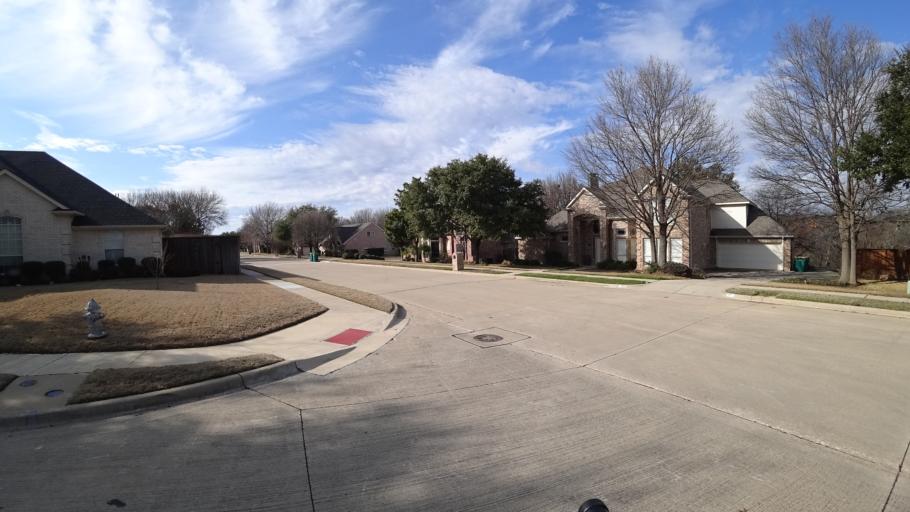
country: US
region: Texas
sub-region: Denton County
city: Lewisville
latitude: 33.0170
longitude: -97.0110
